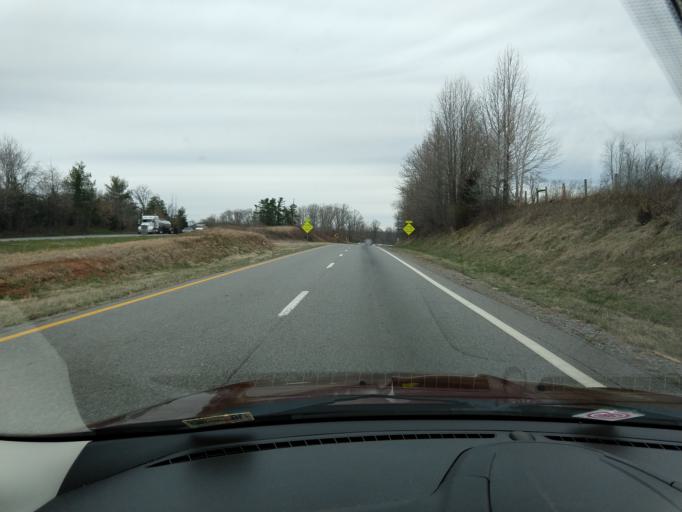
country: US
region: Virginia
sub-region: Franklin County
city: Henry Fork
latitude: 36.8716
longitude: -79.8704
